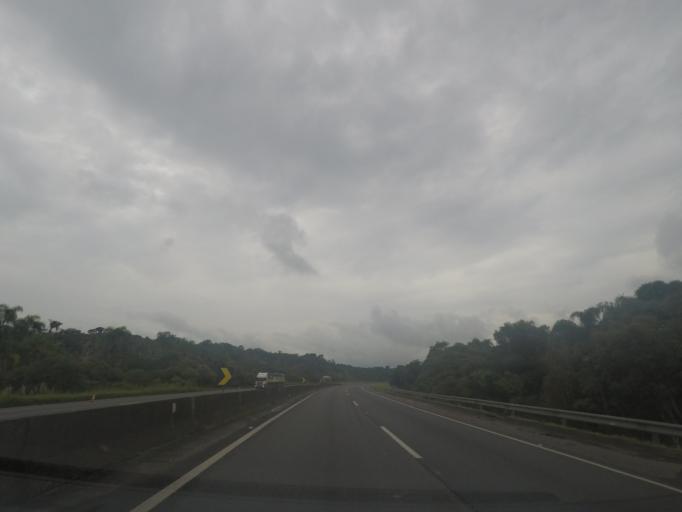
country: BR
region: Sao Paulo
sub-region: Cajati
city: Cajati
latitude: -24.9210
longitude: -48.2594
